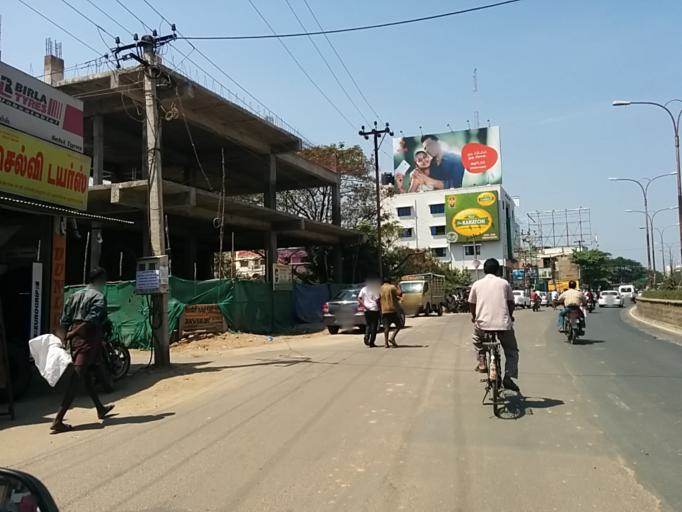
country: IN
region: Pondicherry
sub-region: Puducherry
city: Puducherry
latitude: 11.9274
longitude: 79.8074
